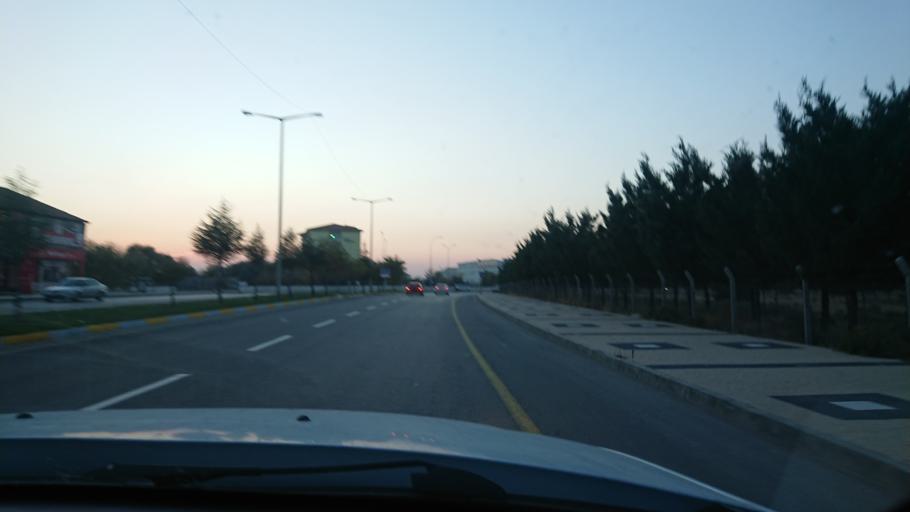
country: TR
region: Aksaray
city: Aksaray
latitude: 38.3570
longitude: 33.9845
